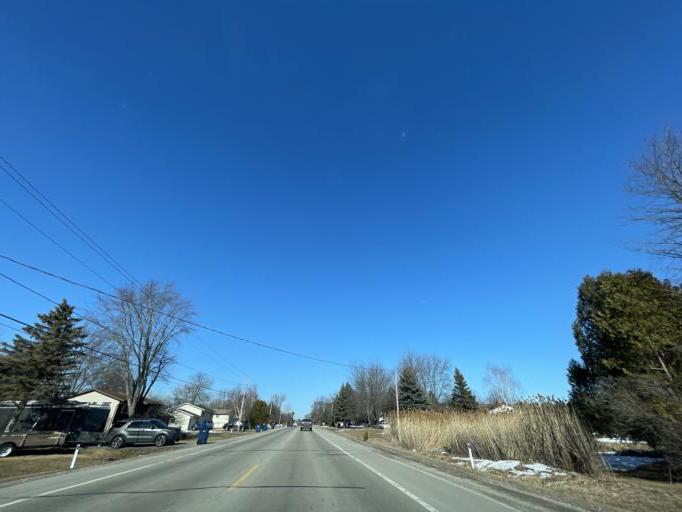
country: US
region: Wisconsin
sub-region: Brown County
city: Suamico
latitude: 44.6216
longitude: -88.0638
